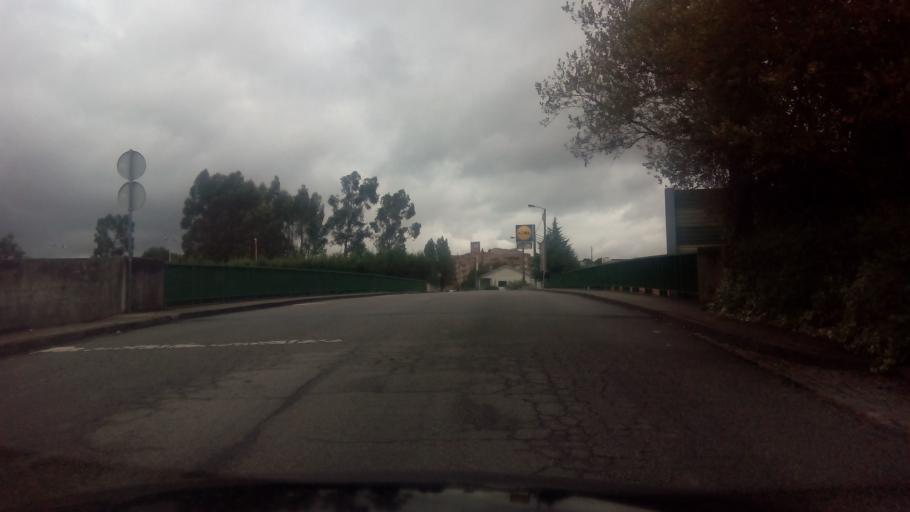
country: PT
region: Porto
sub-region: Paredes
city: Casteloes de Cepeda
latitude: 41.1981
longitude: -8.3347
